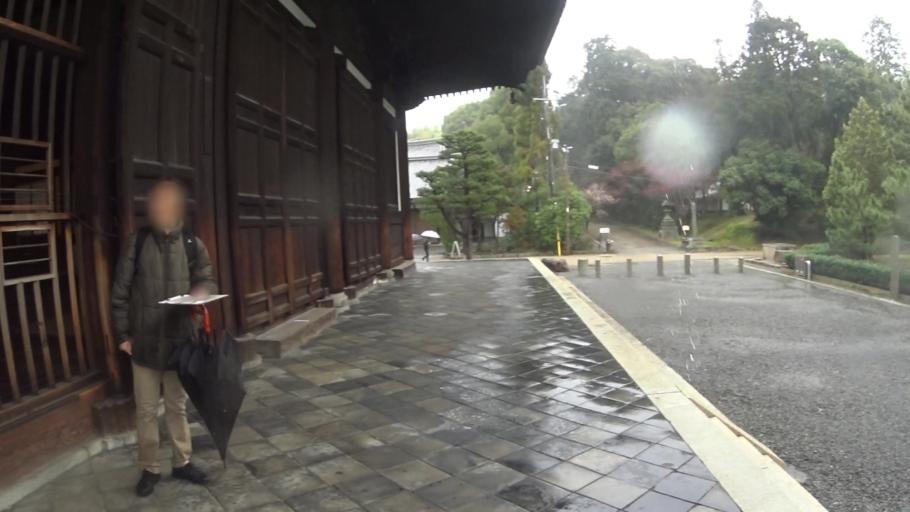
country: JP
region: Kyoto
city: Kyoto
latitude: 34.9757
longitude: 135.7736
